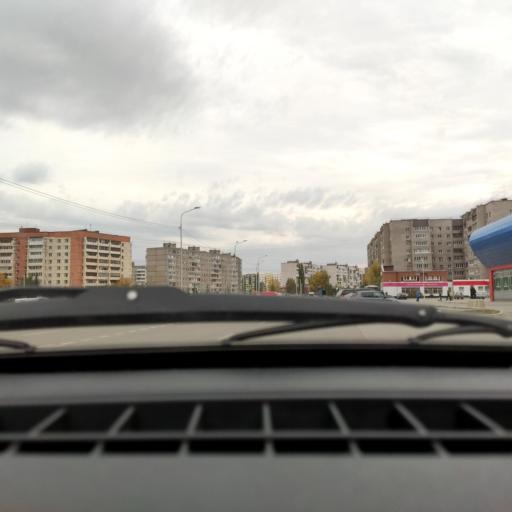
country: RU
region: Bashkortostan
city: Ufa
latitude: 54.7813
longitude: 56.1155
